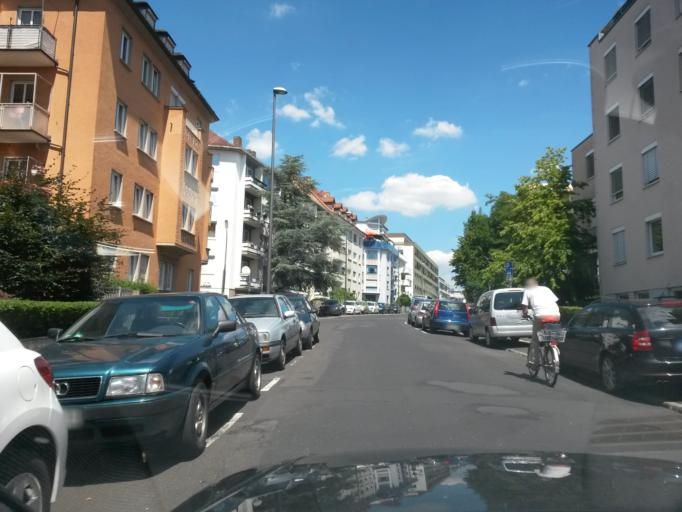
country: DE
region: Bavaria
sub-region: Regierungsbezirk Unterfranken
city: Wuerzburg
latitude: 49.7856
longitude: 9.9387
